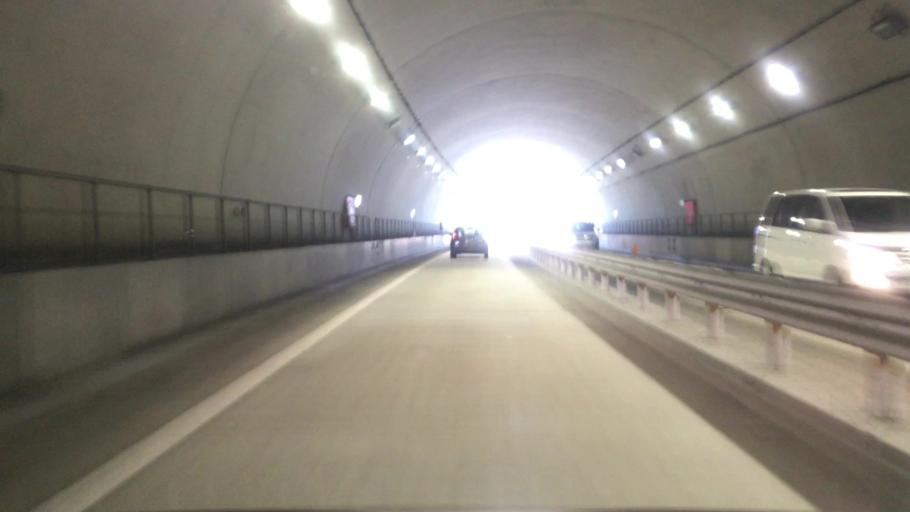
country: JP
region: Tottori
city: Tottori
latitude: 35.5714
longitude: 134.3132
